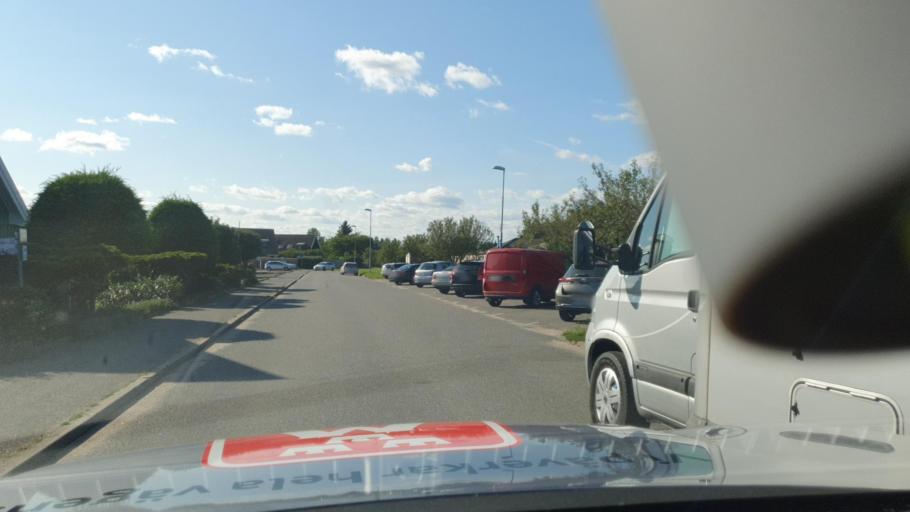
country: SE
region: Skane
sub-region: Bromolla Kommun
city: Bromoella
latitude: 56.0805
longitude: 14.4909
